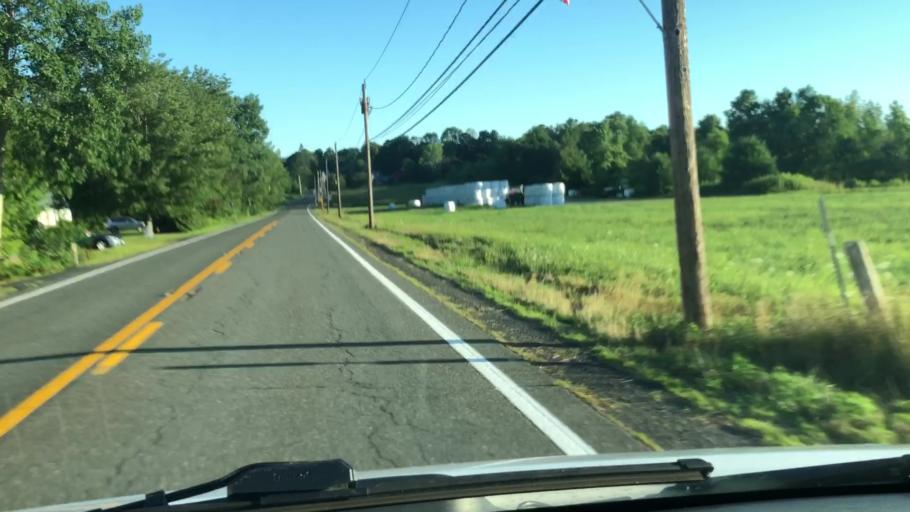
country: US
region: Massachusetts
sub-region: Hampshire County
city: Chesterfield
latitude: 42.3912
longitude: -72.9327
